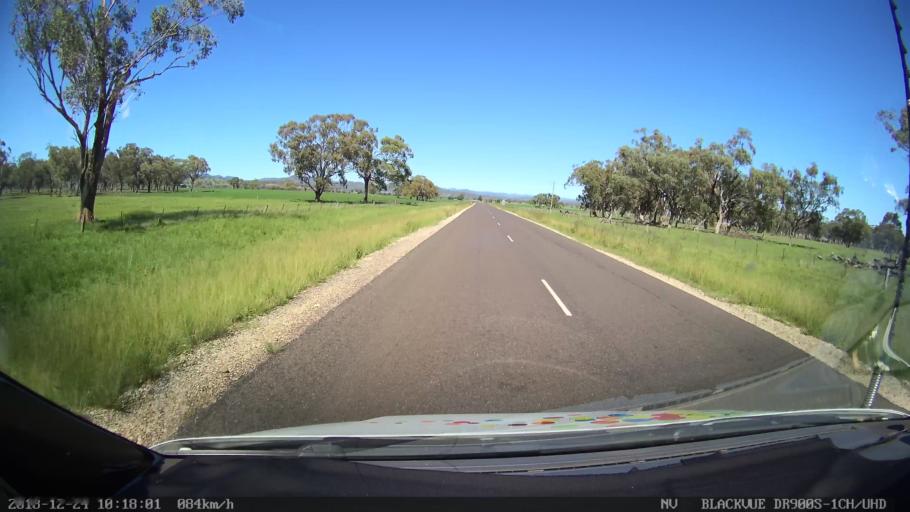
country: AU
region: New South Wales
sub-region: Liverpool Plains
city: Quirindi
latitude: -31.7222
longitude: 150.5826
